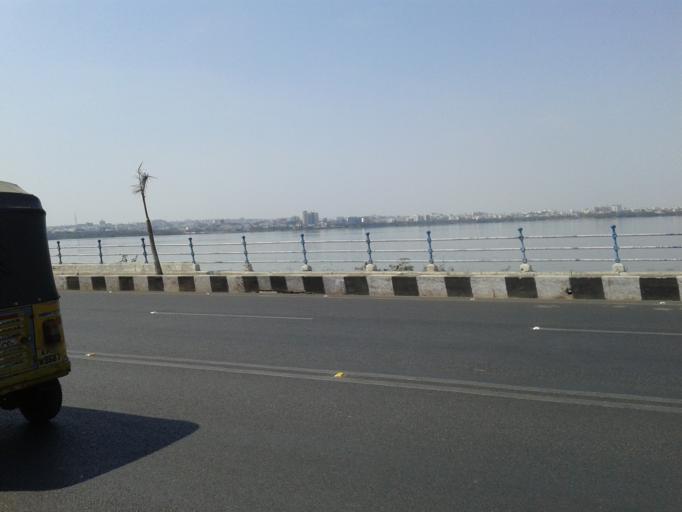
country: IN
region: Telangana
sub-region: Hyderabad
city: Hyderabad
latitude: 17.4193
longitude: 78.4828
